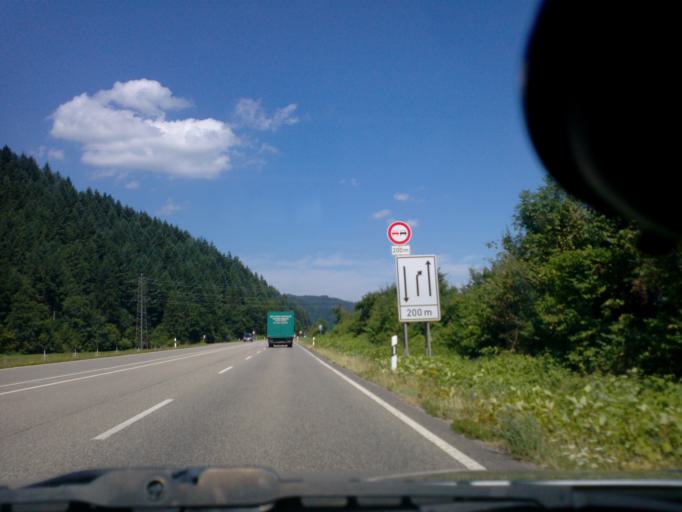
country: DE
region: Baden-Wuerttemberg
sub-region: Freiburg Region
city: Biberach
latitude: 48.3207
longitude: 8.0363
